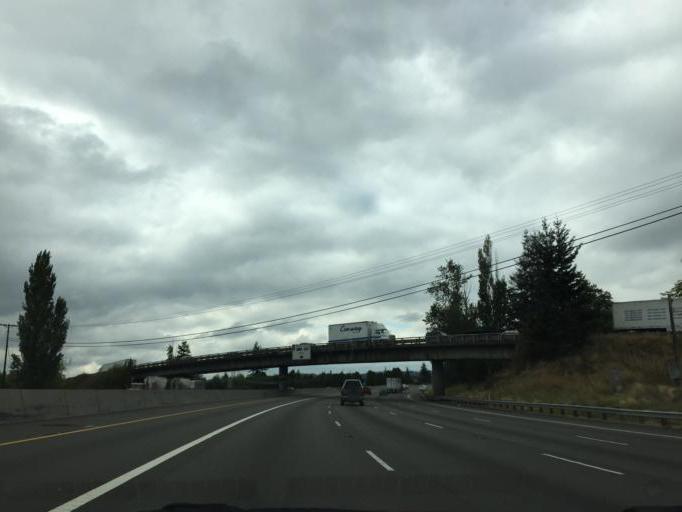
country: US
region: Washington
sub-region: Pierce County
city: Fife Heights
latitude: 47.2442
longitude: -122.3352
